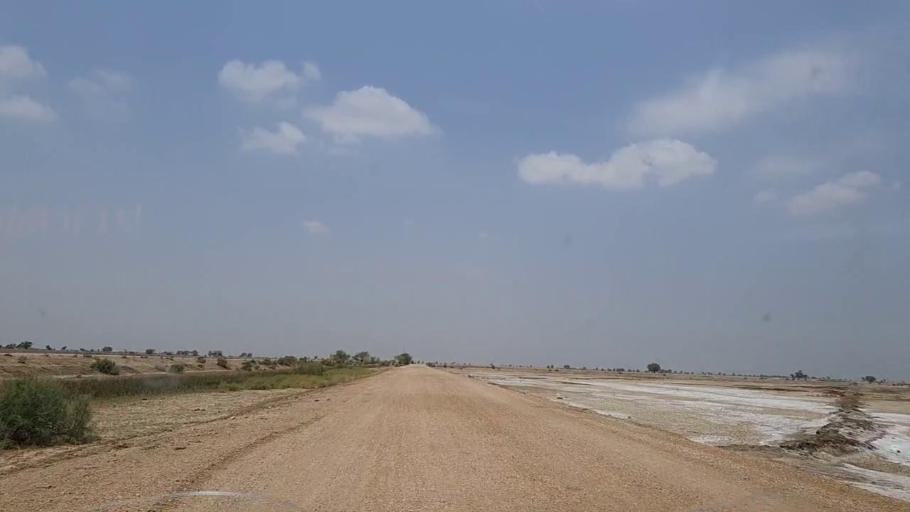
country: PK
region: Sindh
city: Johi
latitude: 26.7627
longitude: 67.6627
